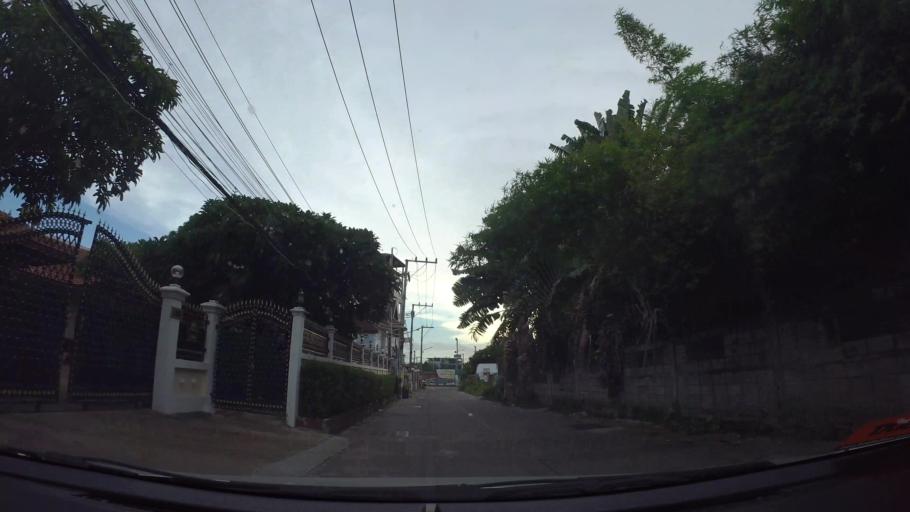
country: TH
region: Chon Buri
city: Phatthaya
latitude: 12.9123
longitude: 100.8850
